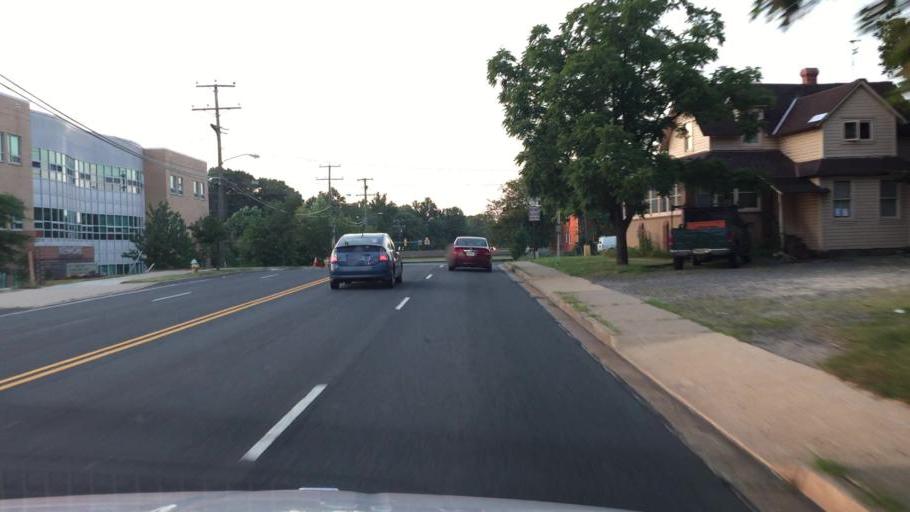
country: US
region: Virginia
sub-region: Fairfax County
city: Baileys Crossroads
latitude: 38.8648
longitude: -77.1286
